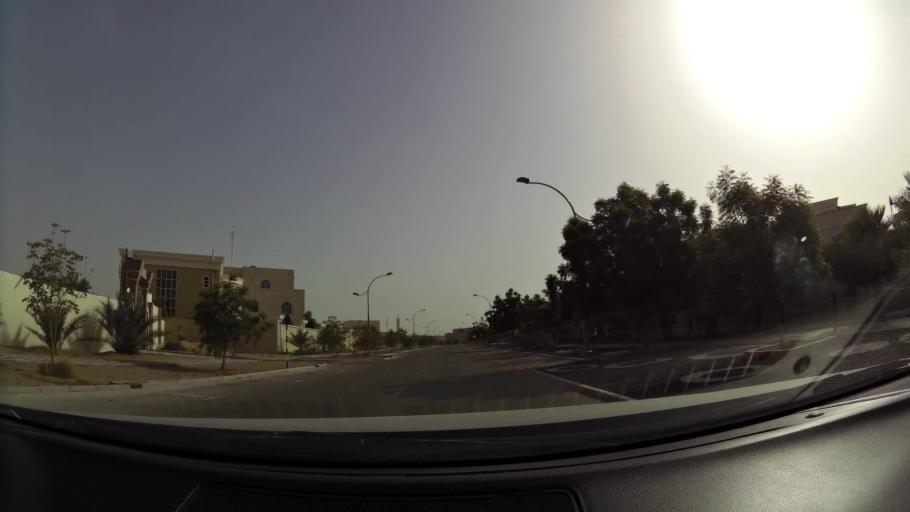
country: AE
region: Abu Dhabi
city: Al Ain
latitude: 24.1503
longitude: 55.7244
